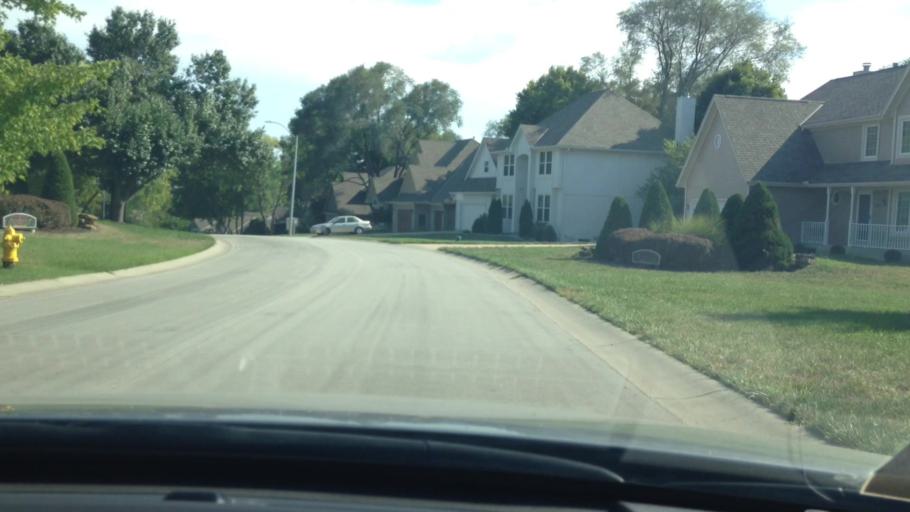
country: US
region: Missouri
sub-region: Jackson County
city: Lees Summit
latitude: 38.9258
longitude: -94.4193
